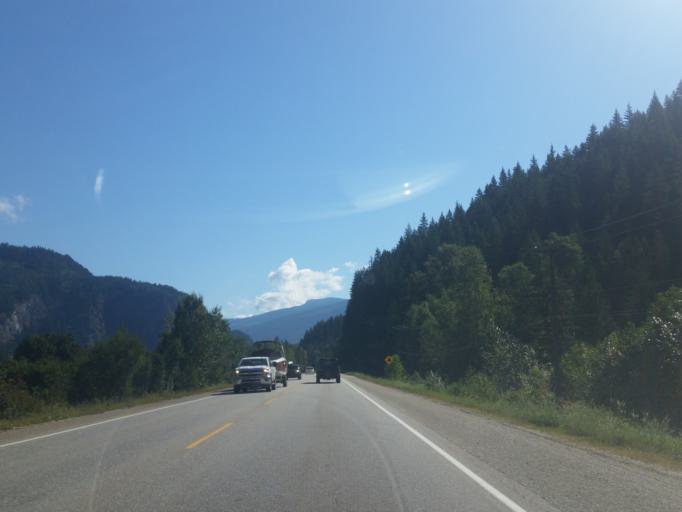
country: CA
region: British Columbia
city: Sicamous
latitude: 50.8861
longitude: -118.8954
